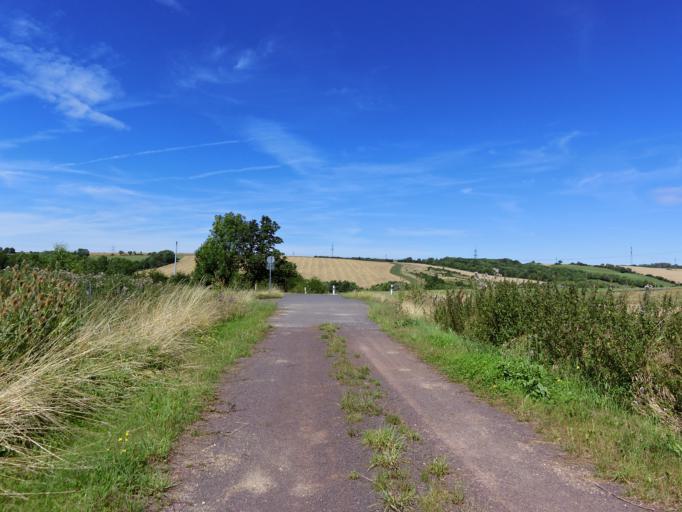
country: DE
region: Thuringia
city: Haina
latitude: 50.9722
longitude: 10.4642
